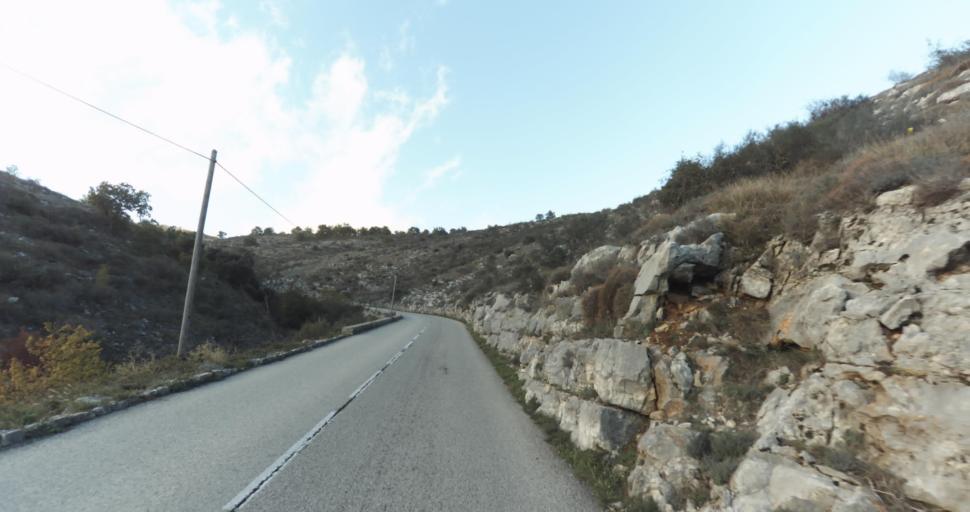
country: FR
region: Provence-Alpes-Cote d'Azur
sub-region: Departement des Alpes-Maritimes
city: Vence
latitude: 43.7534
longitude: 7.0945
